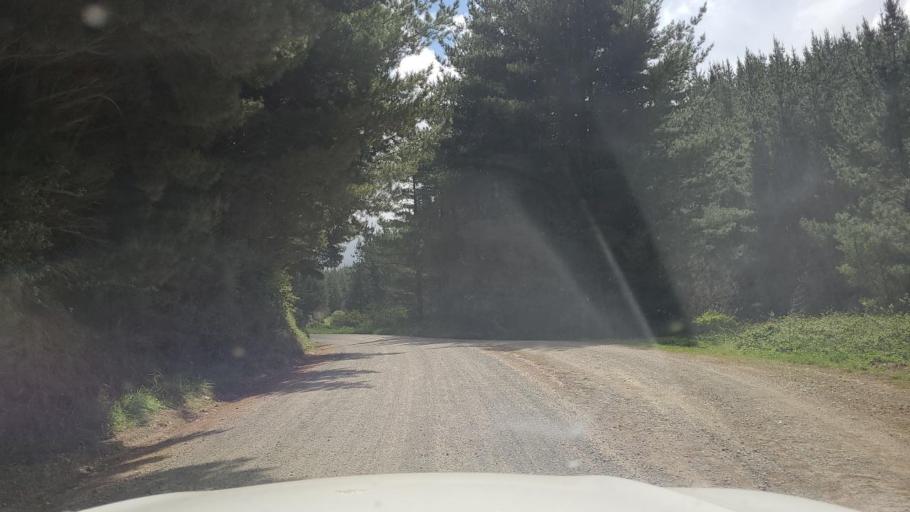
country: NZ
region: Hawke's Bay
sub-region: Napier City
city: Taradale
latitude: -39.2753
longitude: 176.6657
